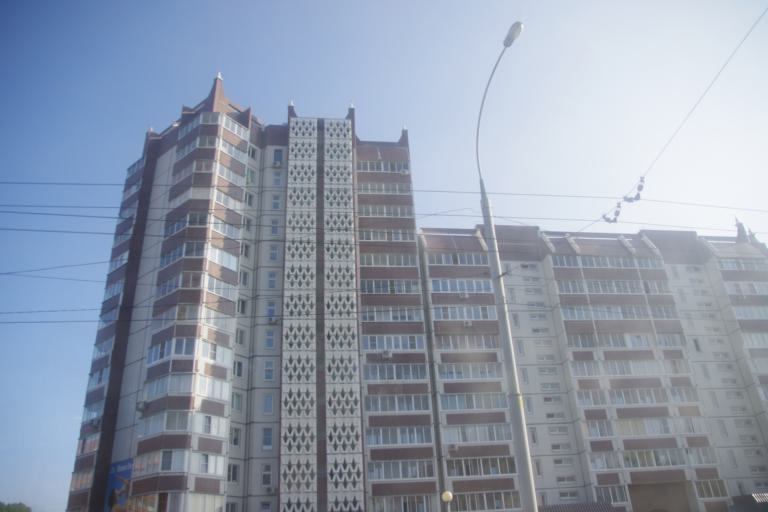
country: RU
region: Samara
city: Tol'yatti
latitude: 53.5046
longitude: 49.2985
